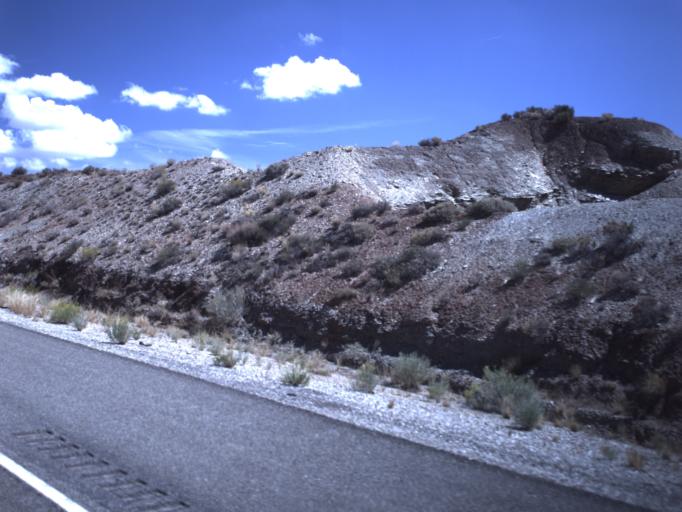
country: US
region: Utah
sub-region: Emery County
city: Ferron
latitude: 38.8467
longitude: -111.0231
